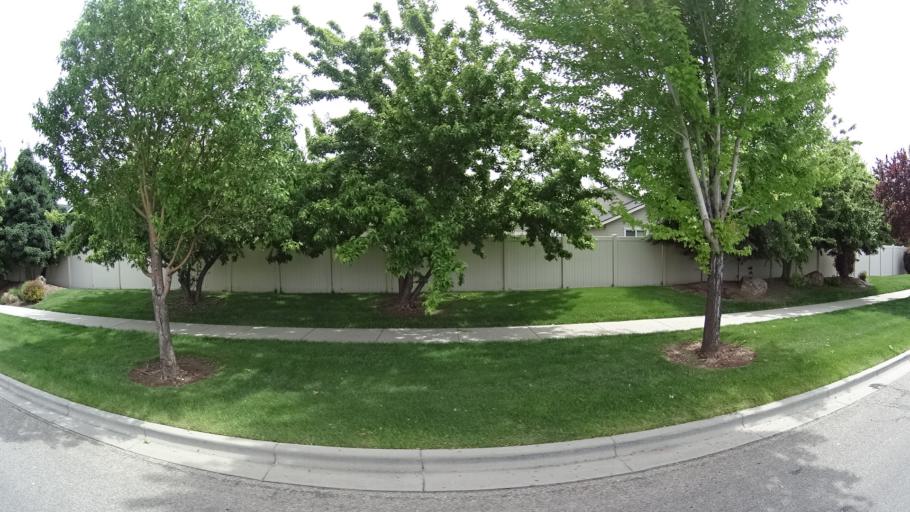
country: US
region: Idaho
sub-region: Ada County
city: Meridian
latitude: 43.5516
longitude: -116.3243
